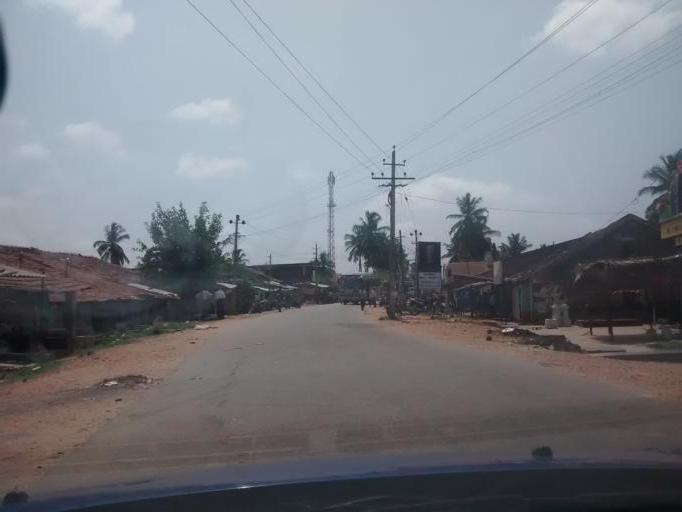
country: IN
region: Karnataka
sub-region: Hassan
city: Konanur
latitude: 12.5812
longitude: 76.2065
